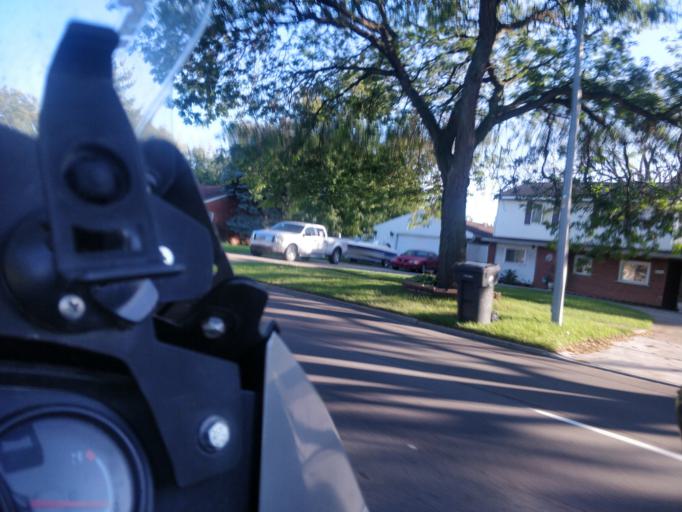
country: US
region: Michigan
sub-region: Wayne County
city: Melvindale
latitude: 42.2713
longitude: -83.1905
